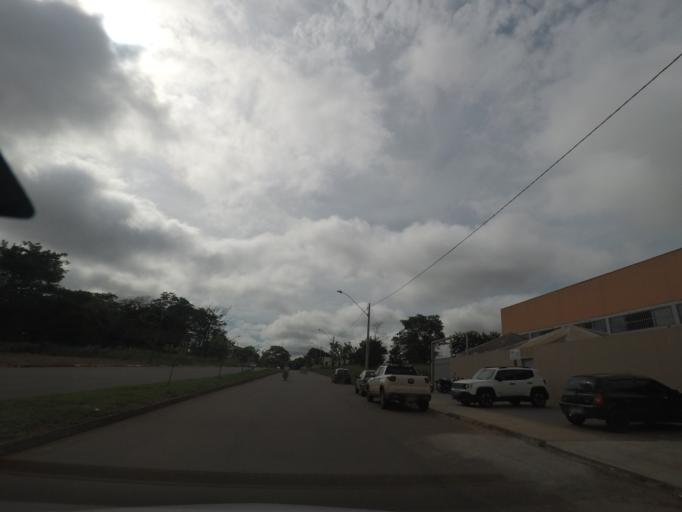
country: BR
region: Goias
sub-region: Goiania
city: Goiania
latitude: -16.7426
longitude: -49.3141
